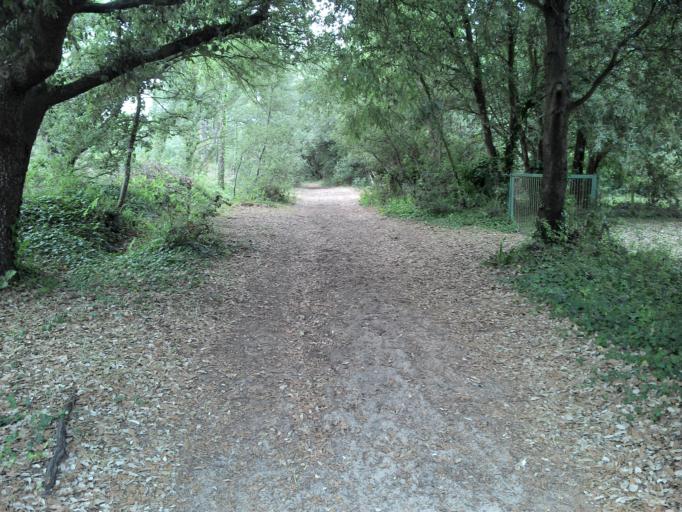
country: FR
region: Poitou-Charentes
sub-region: Departement de la Charente-Maritime
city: Saint-Denis-d'Oleron
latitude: 45.9957
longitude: -1.3814
